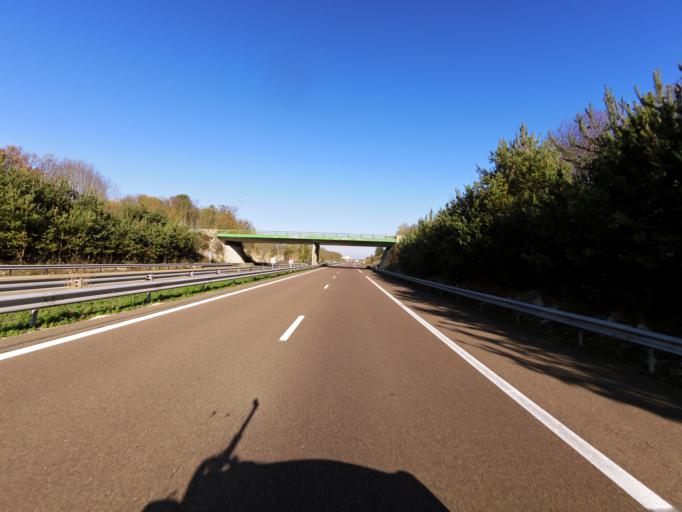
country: FR
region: Champagne-Ardenne
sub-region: Departement de la Marne
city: Fagnieres
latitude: 48.9060
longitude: 4.2846
